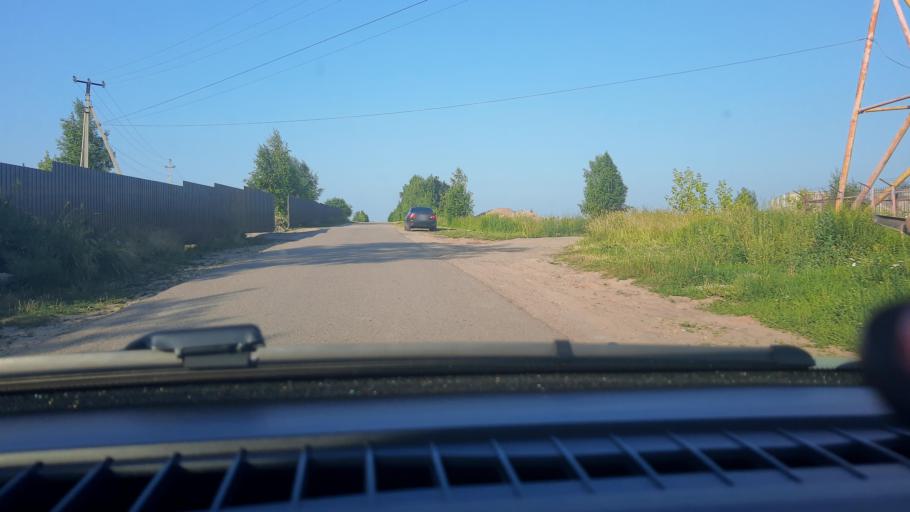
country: RU
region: Nizjnij Novgorod
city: Nizhniy Novgorod
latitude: 56.1922
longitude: 43.9438
